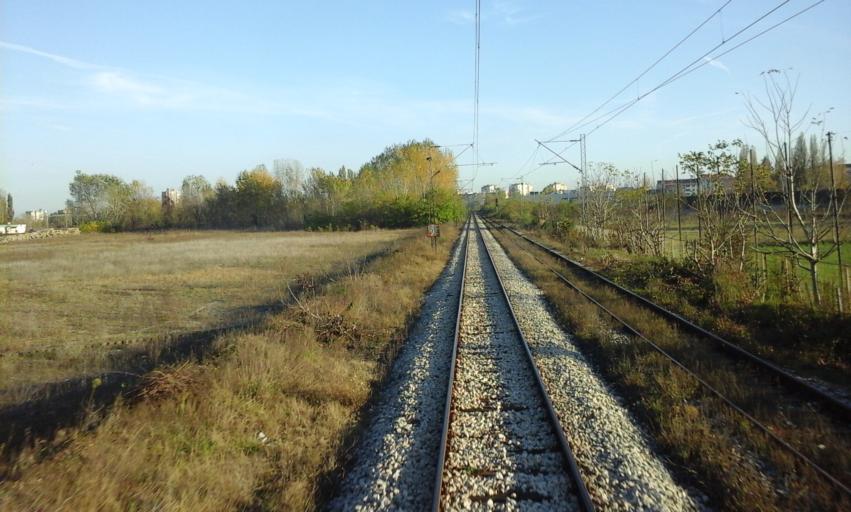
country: RS
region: Autonomna Pokrajina Vojvodina
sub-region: Juznobacki Okrug
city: Novi Sad
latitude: 45.2690
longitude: 19.8132
